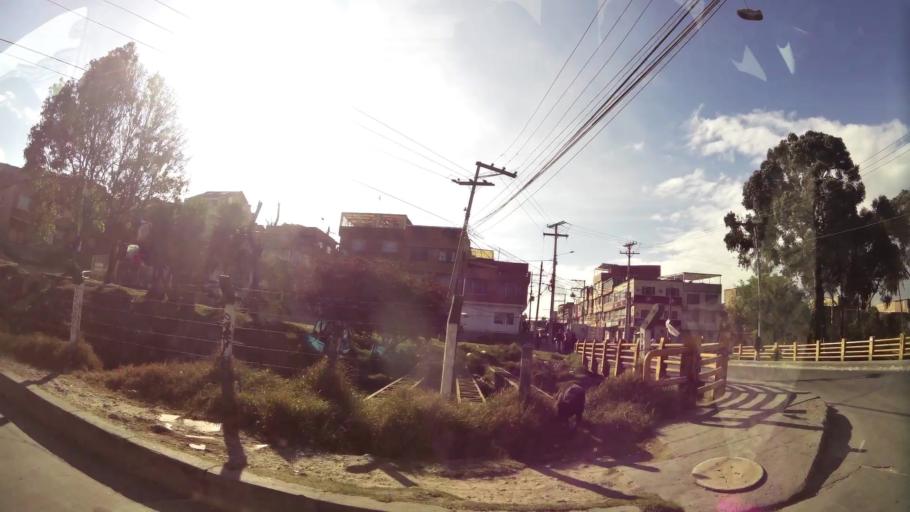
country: CO
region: Cundinamarca
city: Soacha
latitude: 4.5680
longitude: -74.1484
